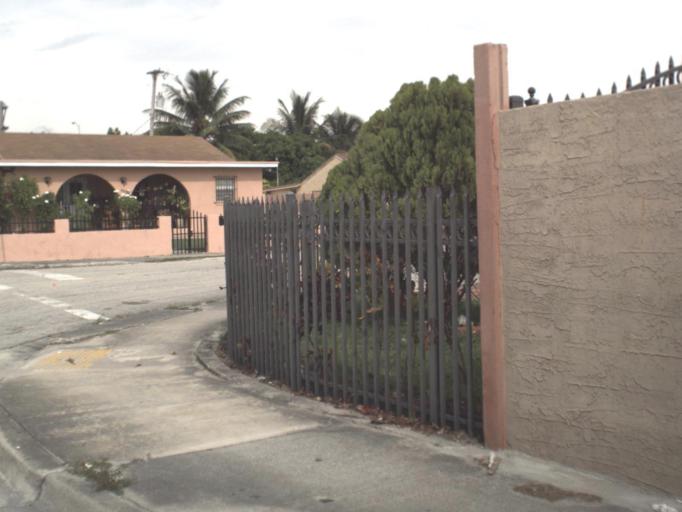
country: US
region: Florida
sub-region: Miami-Dade County
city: Brownsville
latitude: 25.7846
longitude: -80.2558
